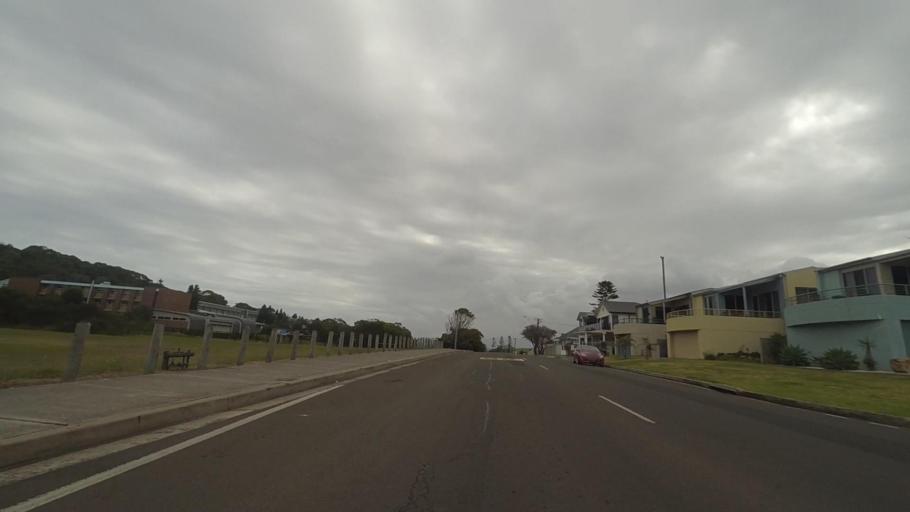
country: AU
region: New South Wales
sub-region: Wollongong
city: Port Kembla
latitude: -34.4875
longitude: 150.9146
